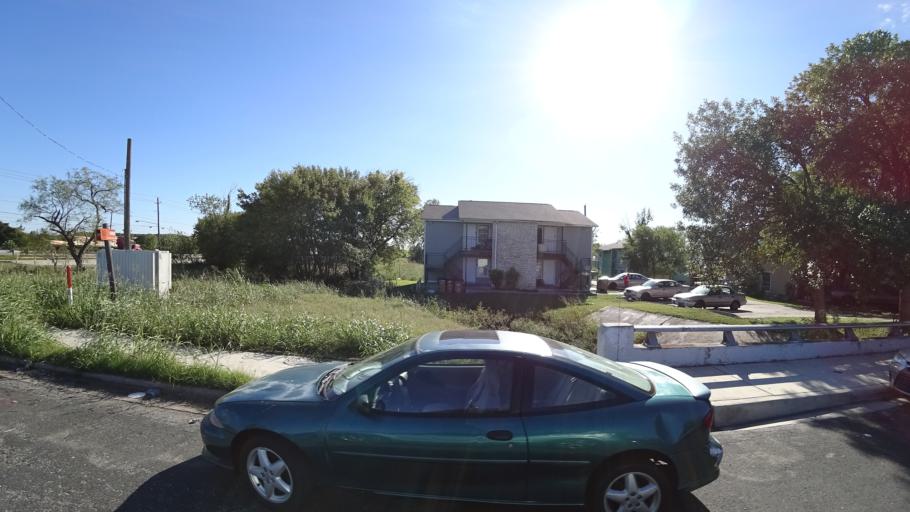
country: US
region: Texas
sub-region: Travis County
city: Hornsby Bend
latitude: 30.2946
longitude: -97.6267
